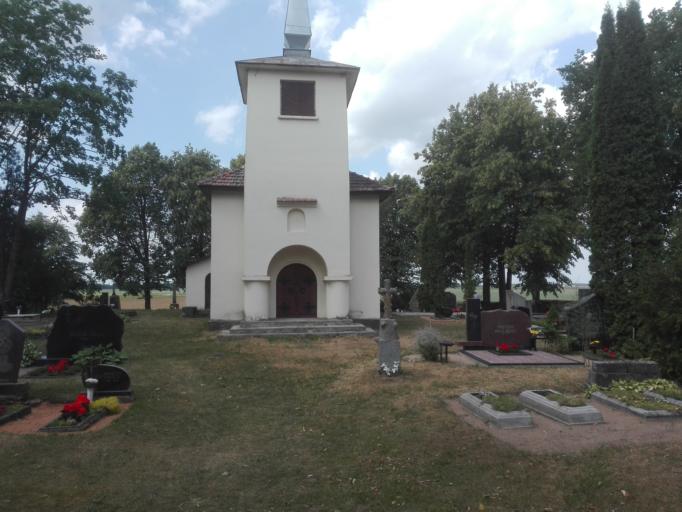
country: LT
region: Panevezys
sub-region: Birzai
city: Birzai
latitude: 56.1157
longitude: 24.8849
